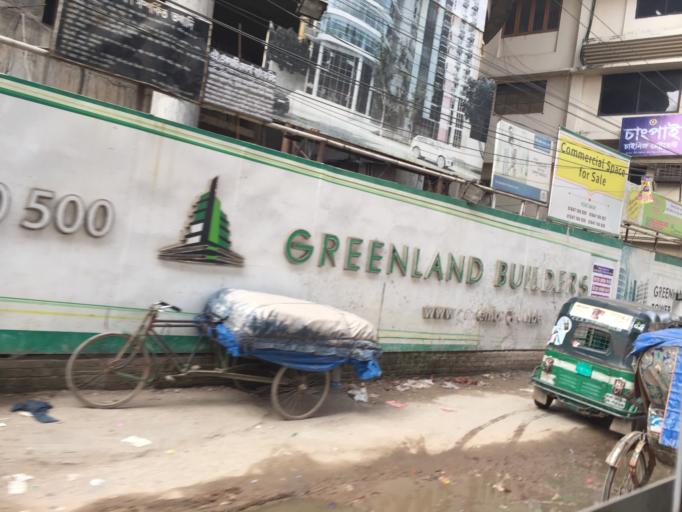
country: BD
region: Dhaka
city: Paltan
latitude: 23.7467
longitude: 90.4106
